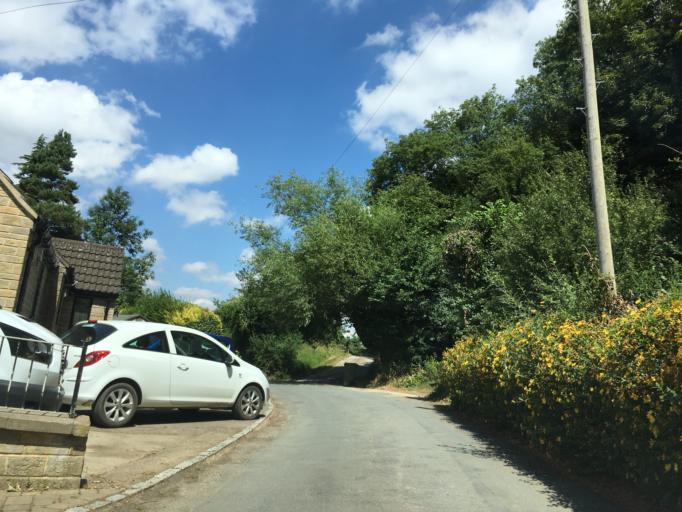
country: GB
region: England
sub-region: Gloucestershire
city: Shurdington
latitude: 51.8440
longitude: -2.1175
